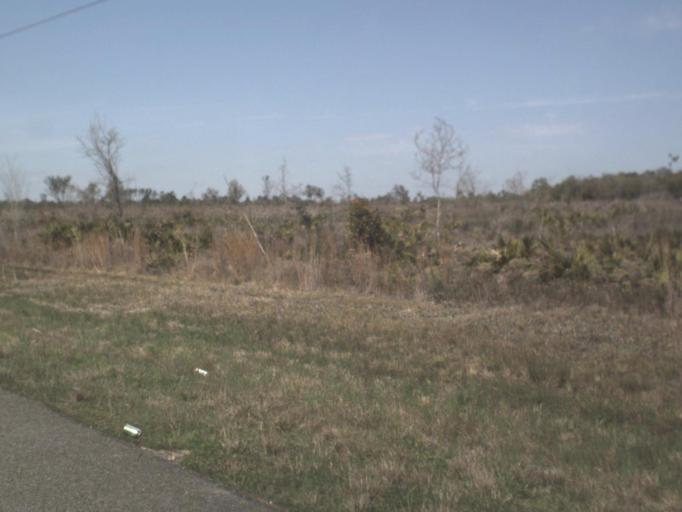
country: US
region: Florida
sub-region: Liberty County
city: Bristol
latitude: 30.5055
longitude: -84.8623
